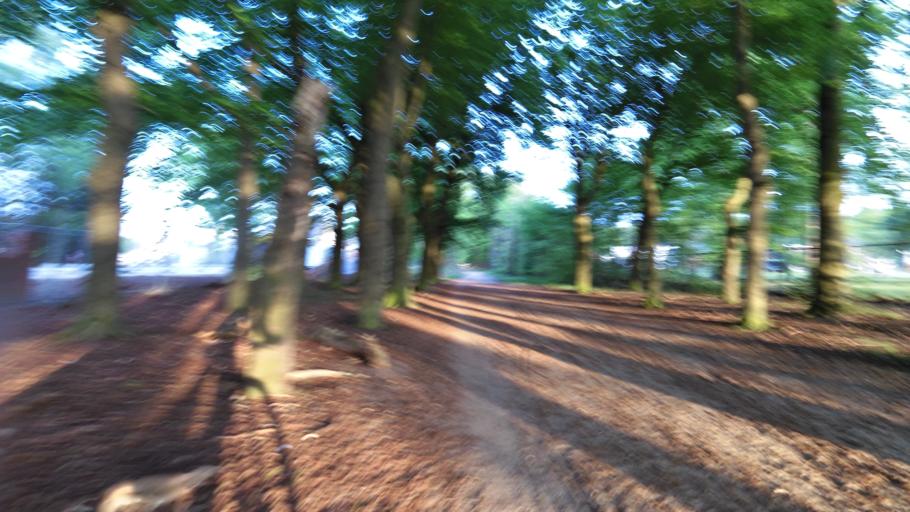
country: NL
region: Gelderland
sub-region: Gemeente Ede
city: Ede
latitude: 52.0374
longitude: 5.6873
